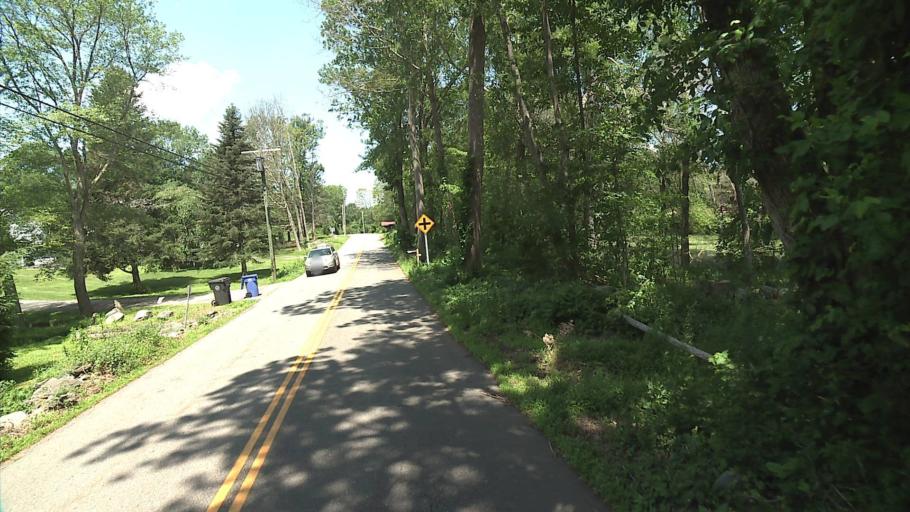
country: US
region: Connecticut
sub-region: New London County
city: Jewett City
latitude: 41.6027
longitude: -71.9090
